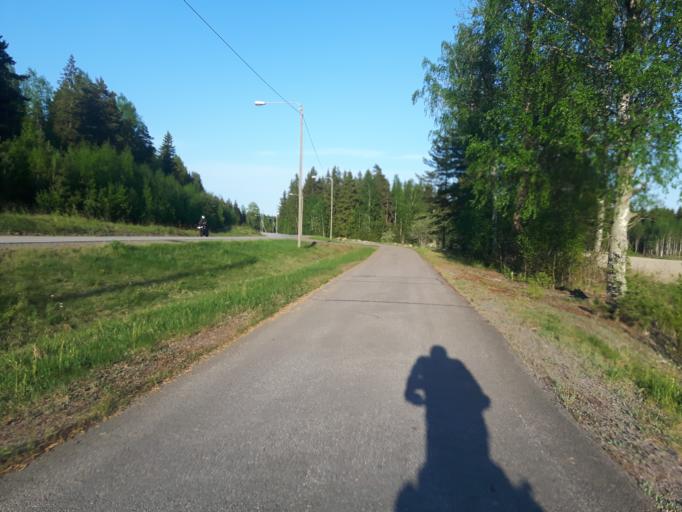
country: FI
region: Uusimaa
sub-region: Loviisa
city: Lovisa
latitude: 60.4557
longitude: 26.1487
